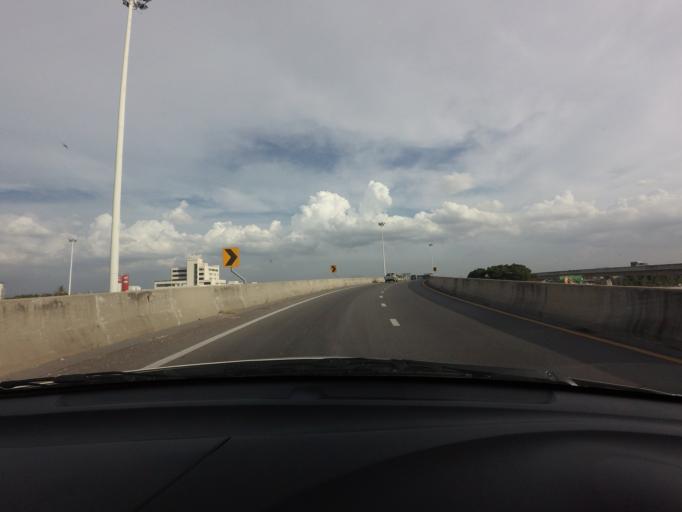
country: TH
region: Nonthaburi
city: Bang Bua Thong
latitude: 13.9517
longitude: 100.4595
